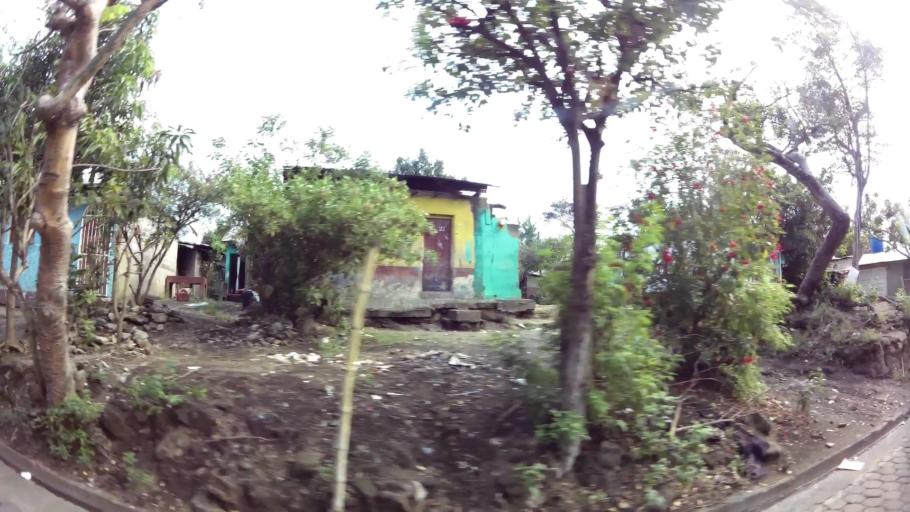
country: NI
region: Masaya
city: Masaya
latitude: 11.9621
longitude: -86.0935
